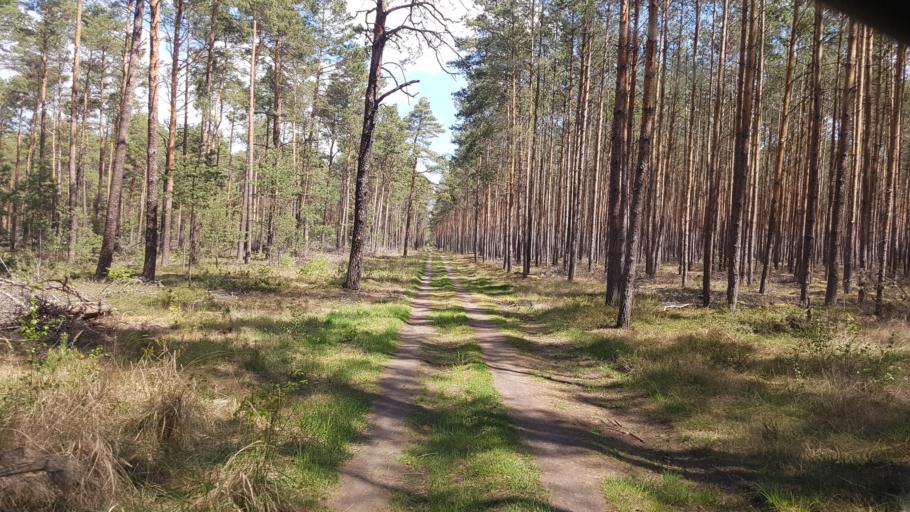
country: DE
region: Brandenburg
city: Sonnewalde
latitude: 51.6499
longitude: 13.6613
